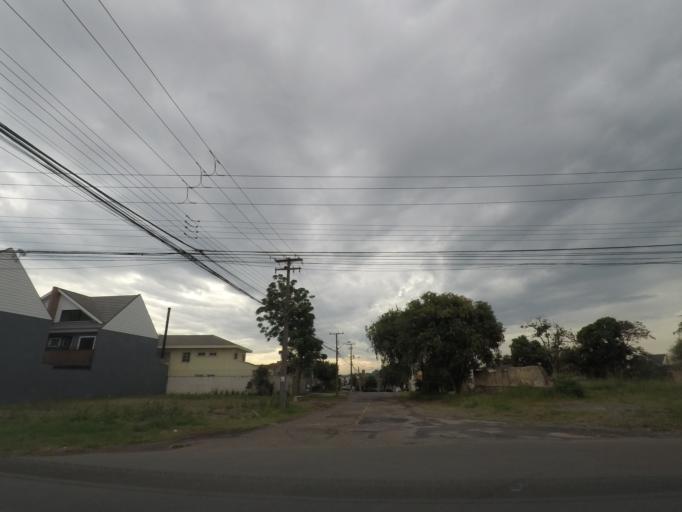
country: BR
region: Parana
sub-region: Curitiba
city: Curitiba
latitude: -25.4739
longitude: -49.3041
